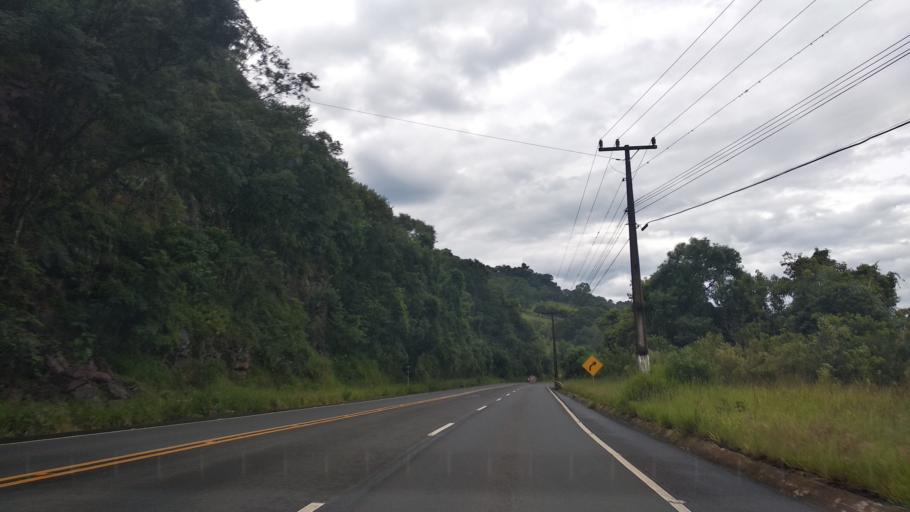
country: BR
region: Santa Catarina
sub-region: Videira
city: Videira
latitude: -27.0632
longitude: -51.2265
